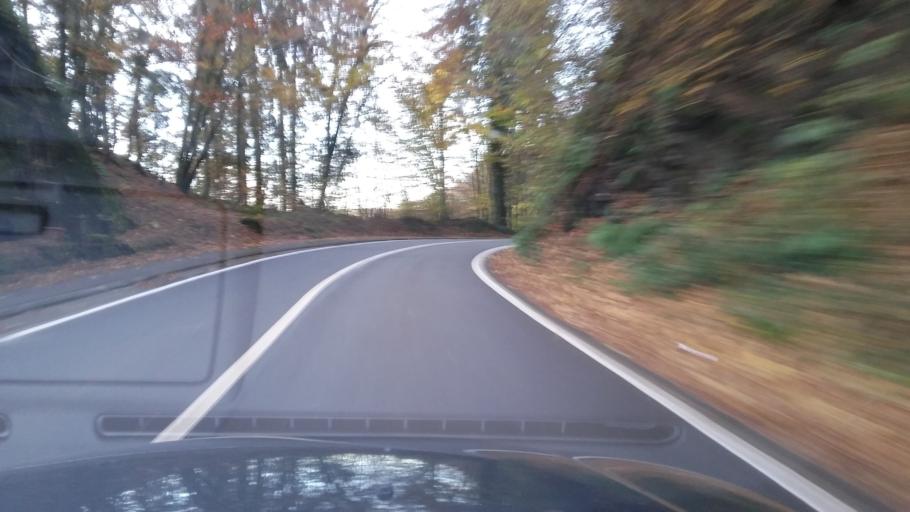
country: BE
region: Wallonia
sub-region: Province du Luxembourg
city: Bouillon
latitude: 49.7853
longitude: 5.0650
